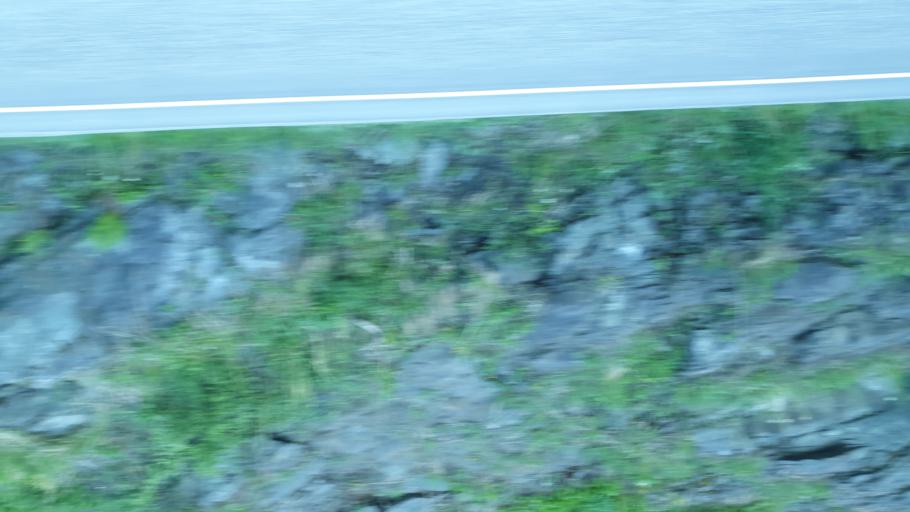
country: NO
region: Sor-Trondelag
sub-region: Rissa
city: Rissa
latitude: 63.5060
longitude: 10.1309
